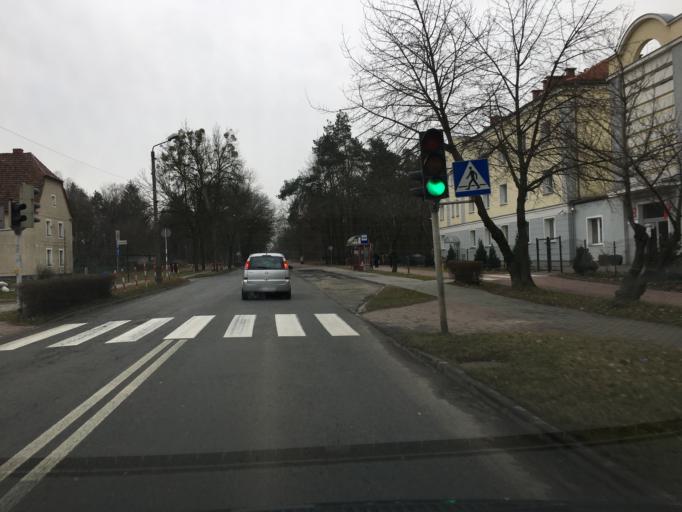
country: PL
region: Opole Voivodeship
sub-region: Powiat kedzierzynsko-kozielski
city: Kedzierzyn-Kozle
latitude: 50.3237
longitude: 18.2424
